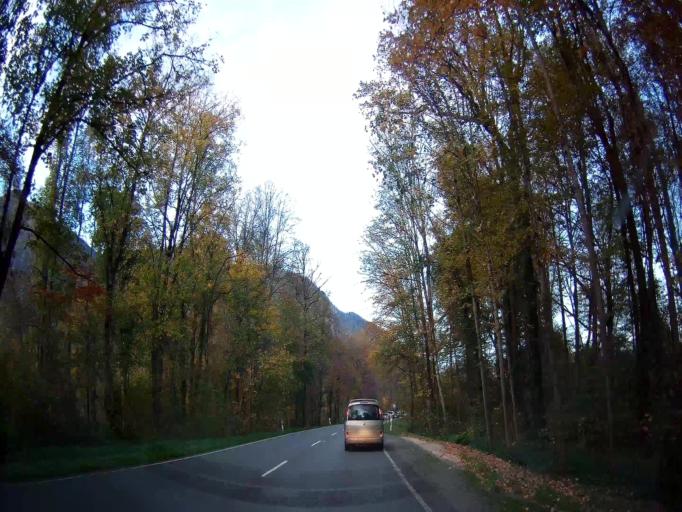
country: DE
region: Bavaria
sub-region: Upper Bavaria
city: Bad Reichenhall
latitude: 47.7288
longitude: 12.8674
